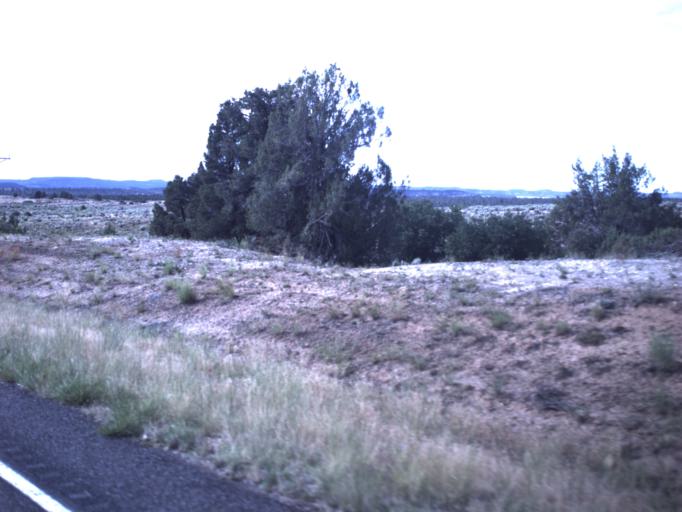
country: US
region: Utah
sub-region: Kane County
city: Kanab
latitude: 37.2437
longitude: -112.7536
